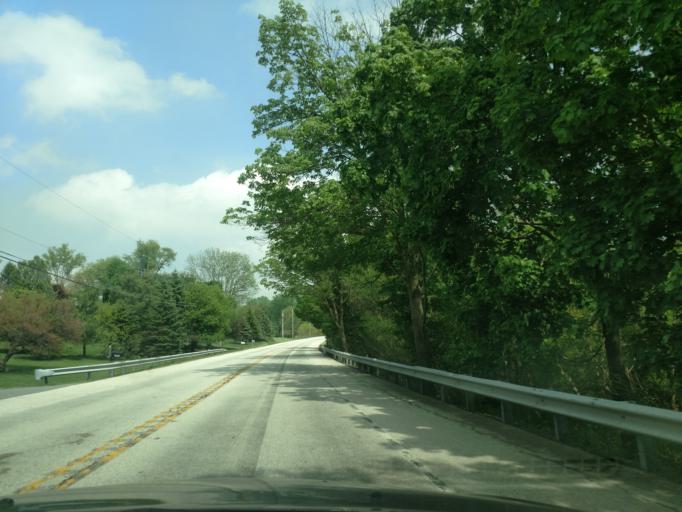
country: US
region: Pennsylvania
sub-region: Chester County
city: Elverson
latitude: 40.1629
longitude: -75.7808
